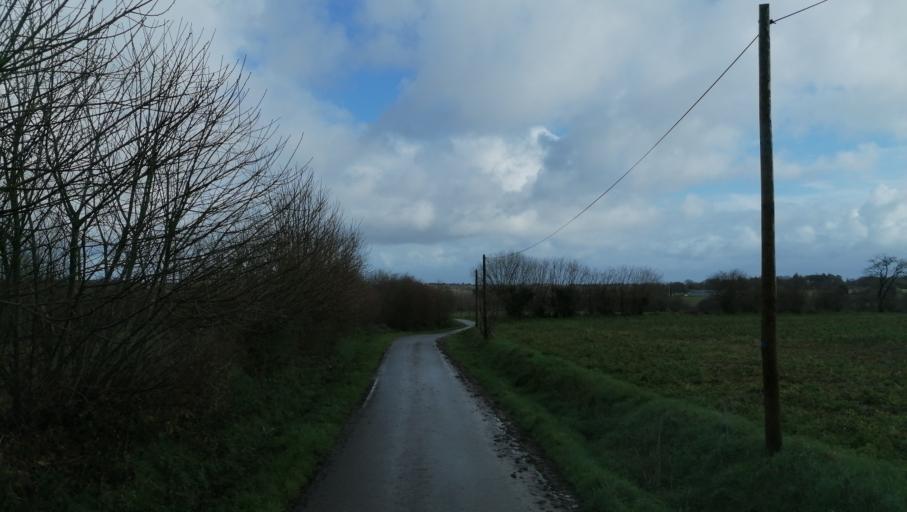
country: FR
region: Brittany
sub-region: Departement des Cotes-d'Armor
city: Lanrodec
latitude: 48.4851
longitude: -3.0411
